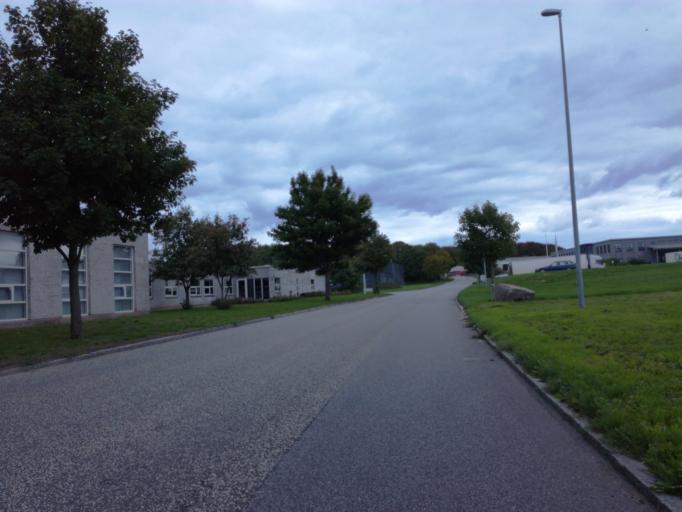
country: DK
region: South Denmark
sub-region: Vejle Kommune
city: Vejle
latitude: 55.6804
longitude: 9.5825
